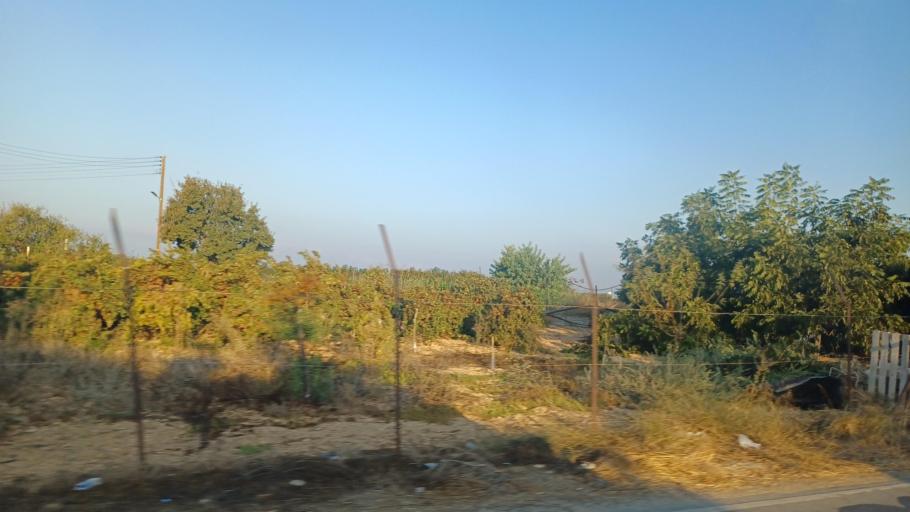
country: CY
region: Pafos
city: Empa
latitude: 34.8014
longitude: 32.4356
